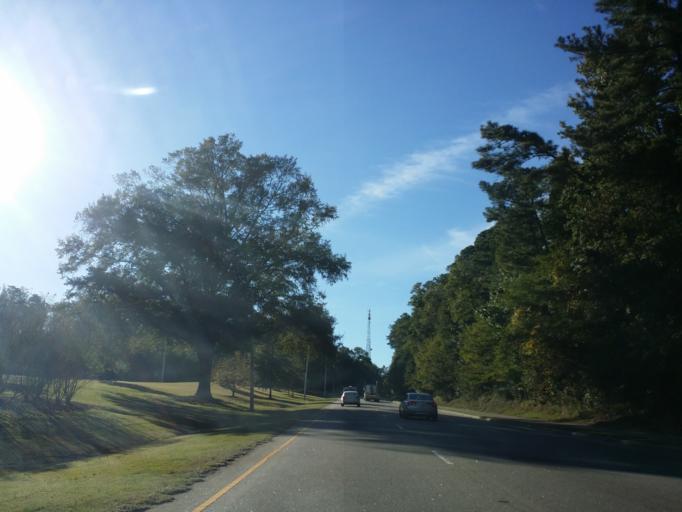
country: US
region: North Carolina
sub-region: Wake County
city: West Raleigh
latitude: 35.7796
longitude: -78.6681
